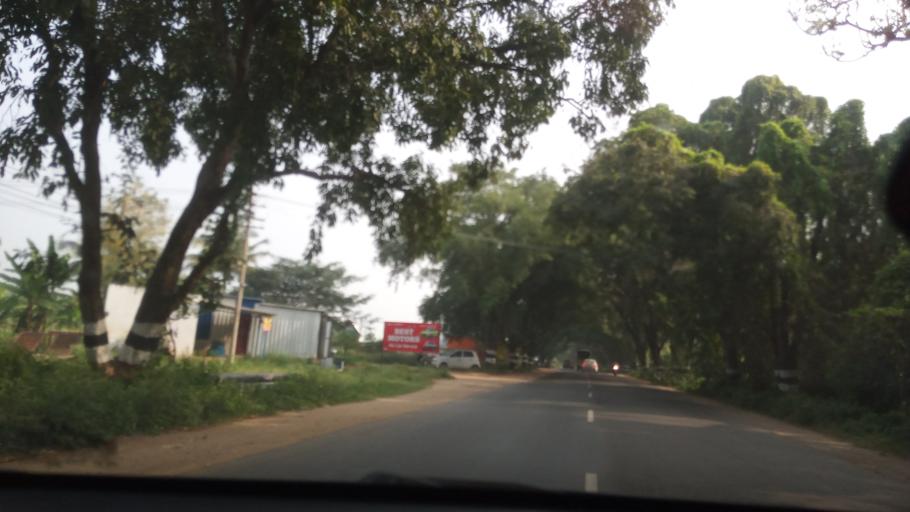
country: IN
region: Tamil Nadu
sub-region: Coimbatore
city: Annur
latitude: 11.1944
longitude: 77.0682
